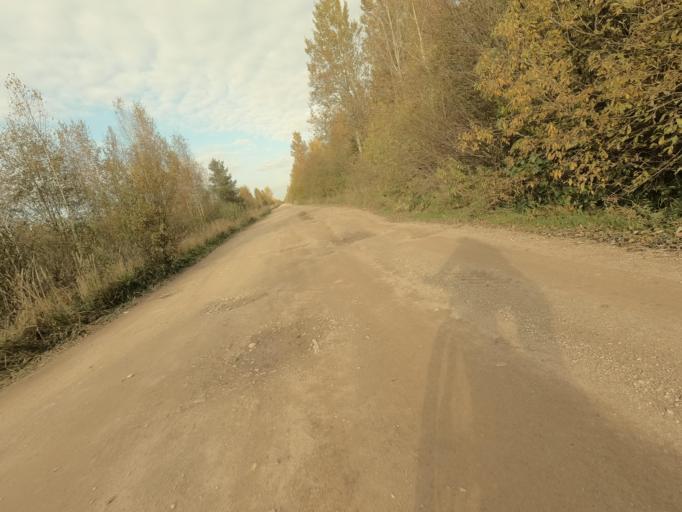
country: RU
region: Novgorod
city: Volkhovskiy
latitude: 58.9049
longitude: 31.0359
